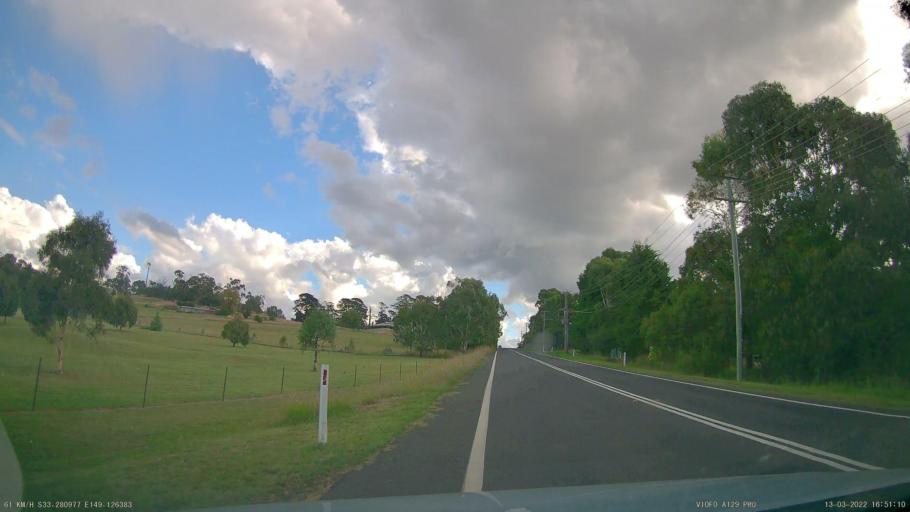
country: AU
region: New South Wales
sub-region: Orange Municipality
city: Orange
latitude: -33.2811
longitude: 149.1261
